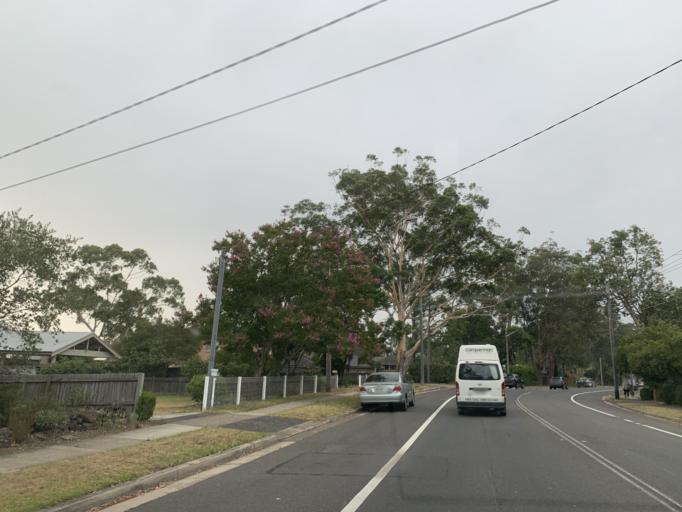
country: AU
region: New South Wales
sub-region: The Hills Shire
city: West Pennant
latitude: -33.7403
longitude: 151.0479
